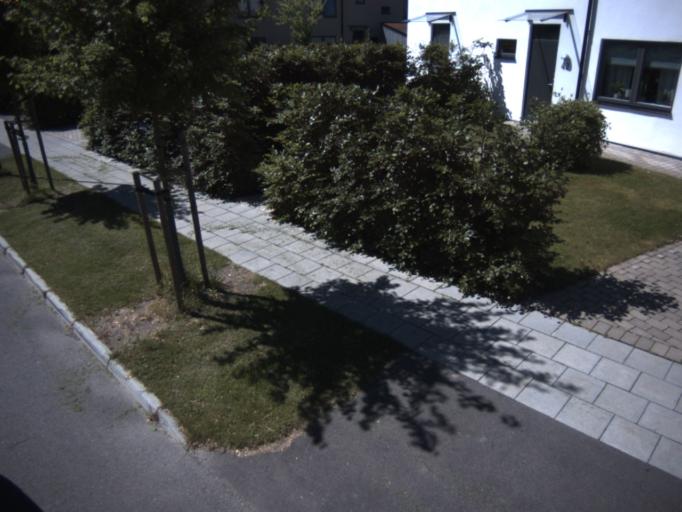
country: SE
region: Skane
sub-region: Helsingborg
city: Helsingborg
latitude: 56.0801
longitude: 12.6981
